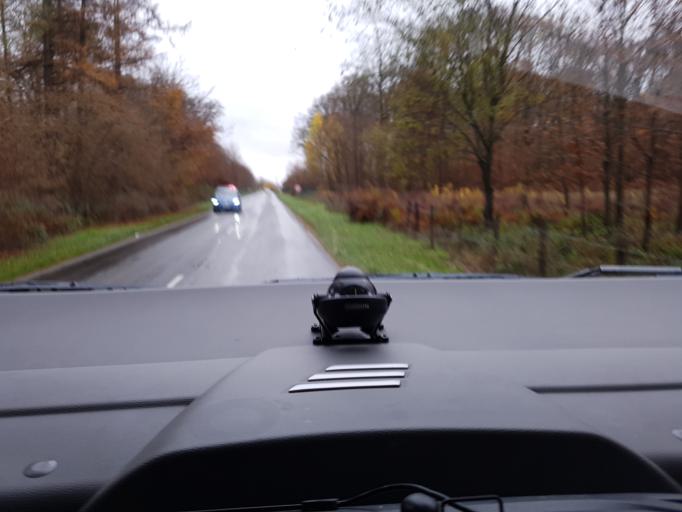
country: FR
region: Haute-Normandie
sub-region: Departement de l'Eure
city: Pont-Saint-Pierre
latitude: 49.3186
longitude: 1.2991
